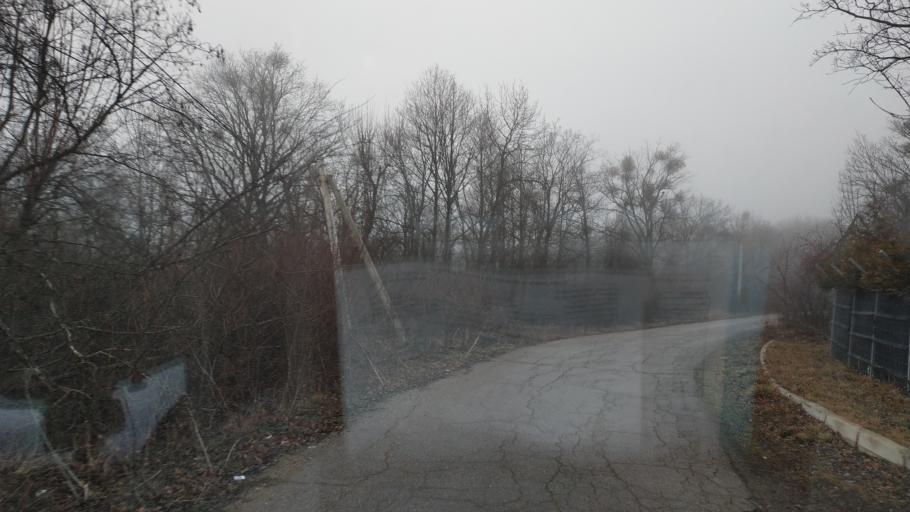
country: MD
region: Laloveni
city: Ialoveni
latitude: 46.9486
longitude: 28.6992
